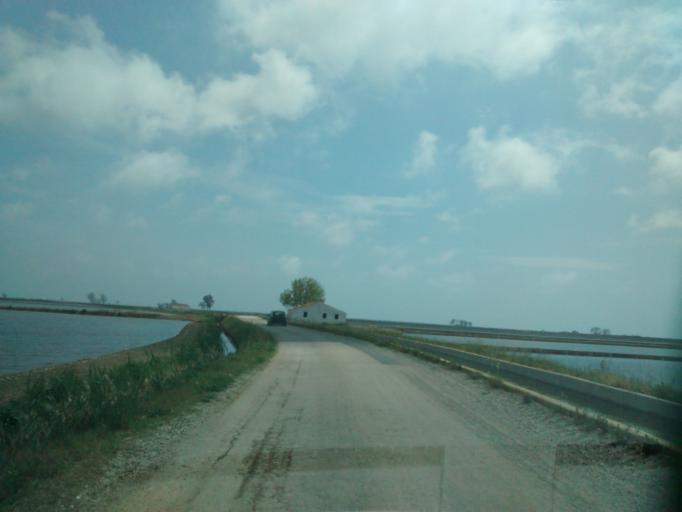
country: ES
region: Catalonia
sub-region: Provincia de Tarragona
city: Deltebre
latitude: 40.6850
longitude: 0.7876
